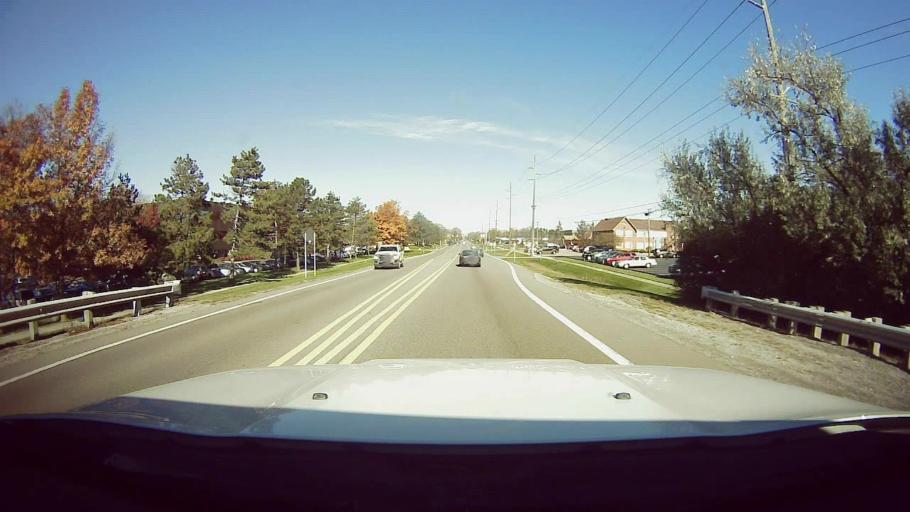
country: US
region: Michigan
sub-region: Oakland County
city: Farmington Hills
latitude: 42.4961
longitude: -83.3780
